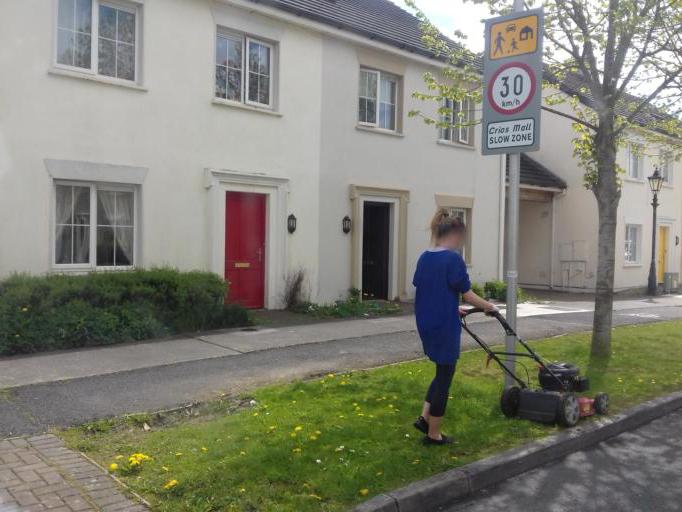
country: IE
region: Leinster
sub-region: Laois
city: Portlaoise
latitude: 53.0493
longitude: -7.3183
